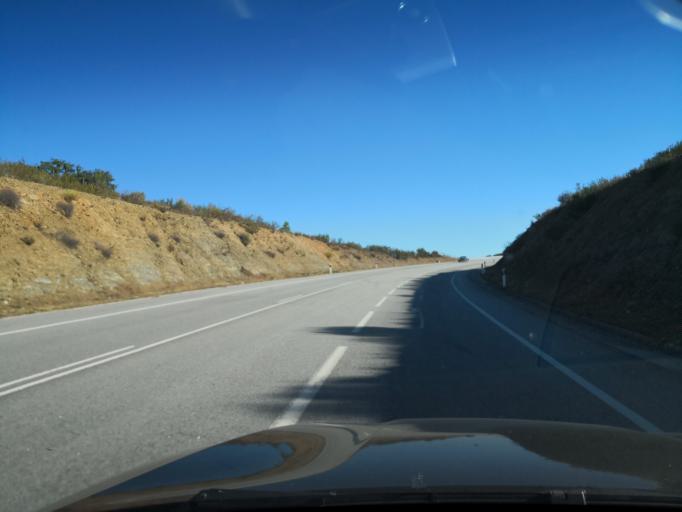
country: PT
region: Braganca
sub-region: Mirandela
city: Mirandela
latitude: 41.4895
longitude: -7.2245
